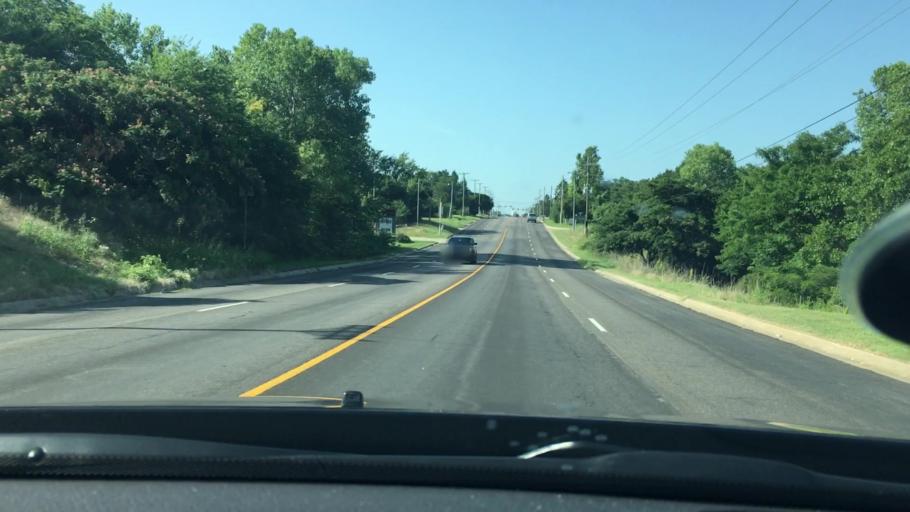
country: US
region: Oklahoma
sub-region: Pontotoc County
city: Ada
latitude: 34.7868
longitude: -96.6349
